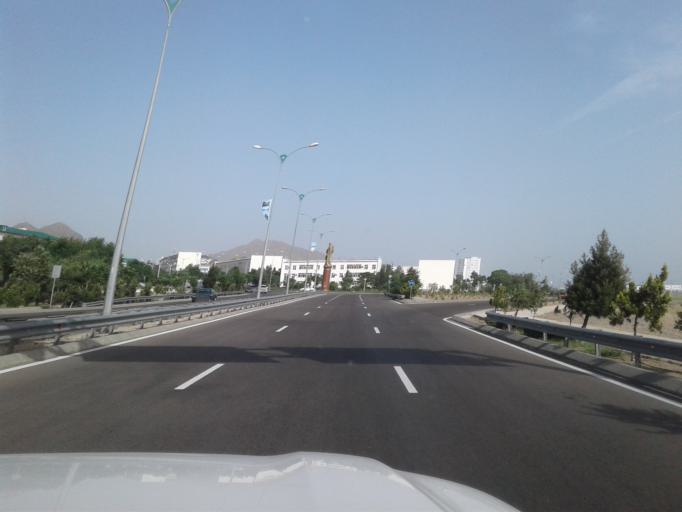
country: TM
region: Balkan
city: Turkmenbasy
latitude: 40.0043
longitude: 52.9515
